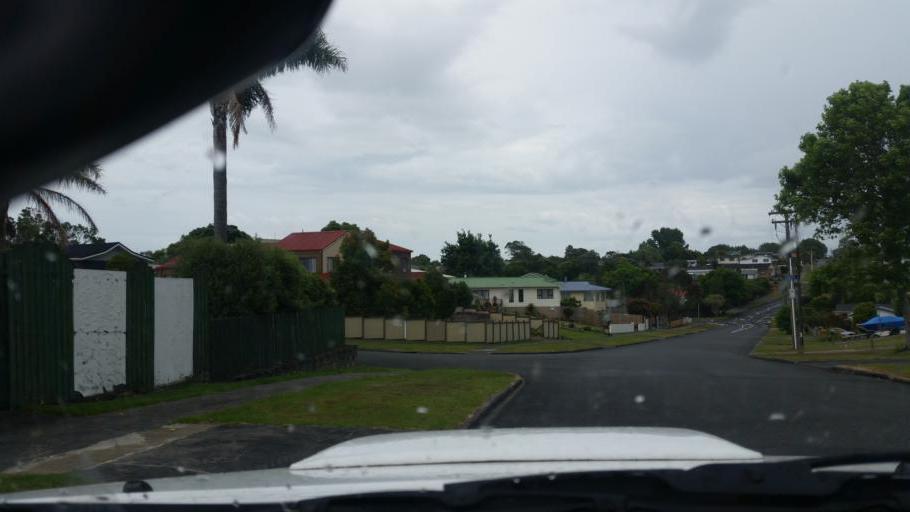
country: NZ
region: Northland
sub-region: Kaipara District
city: Dargaville
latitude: -35.9289
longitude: 173.8642
